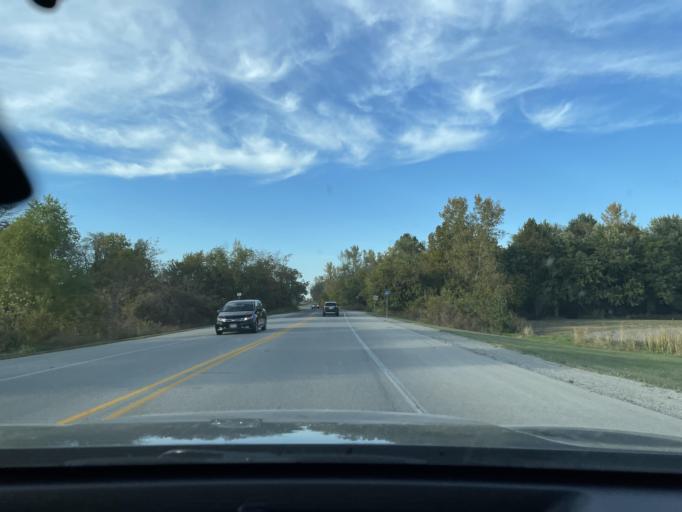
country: US
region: Missouri
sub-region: Andrew County
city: Country Club Village
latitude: 39.7839
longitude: -94.7675
